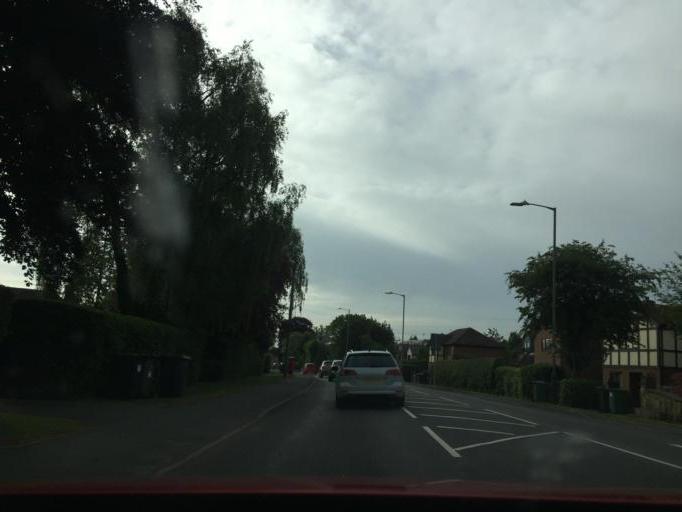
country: GB
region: England
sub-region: Warwickshire
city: Attleborough
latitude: 52.5071
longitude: -1.4403
